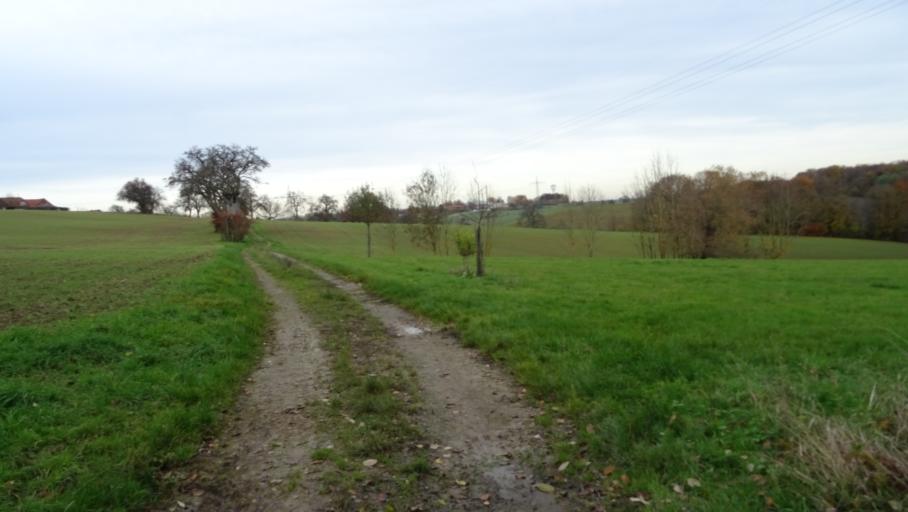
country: DE
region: Baden-Wuerttemberg
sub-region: Karlsruhe Region
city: Mosbach
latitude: 49.3388
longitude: 9.1526
